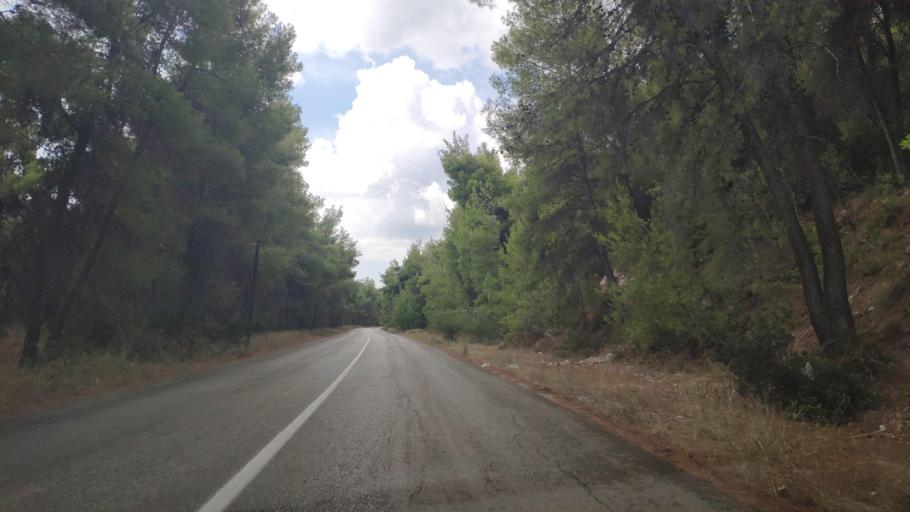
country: GR
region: Central Greece
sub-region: Nomos Fthiotidos
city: Malesina
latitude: 38.6423
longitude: 23.1985
